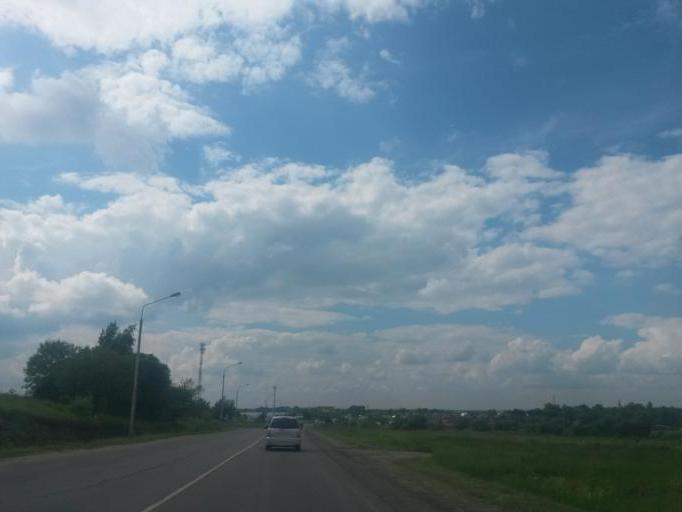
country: RU
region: Moskovskaya
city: Yam
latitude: 55.4835
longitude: 37.7677
